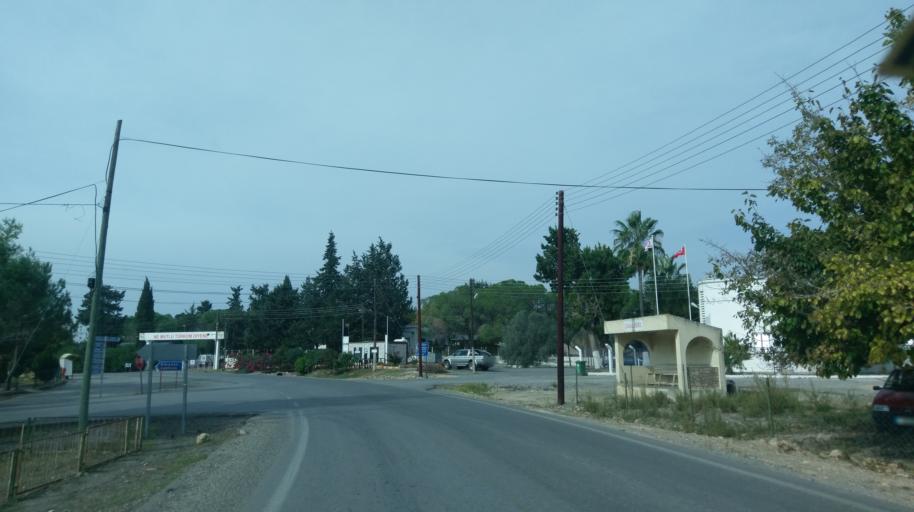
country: CY
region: Keryneia
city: Lapithos
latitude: 35.3146
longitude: 33.0704
